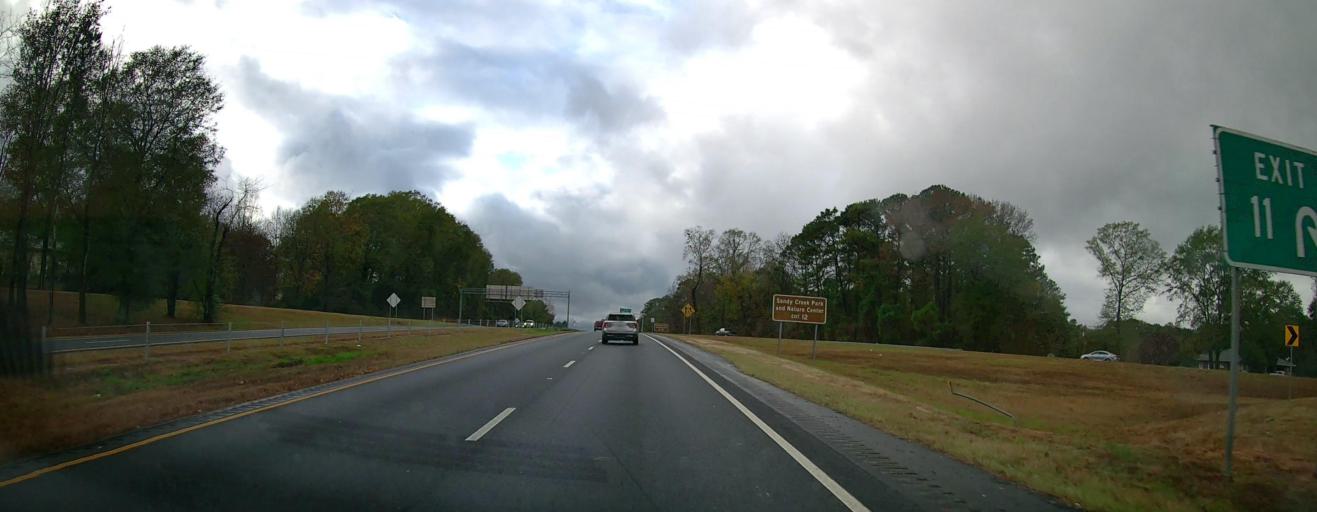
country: US
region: Georgia
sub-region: Clarke County
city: Athens
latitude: 33.9786
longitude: -83.3643
